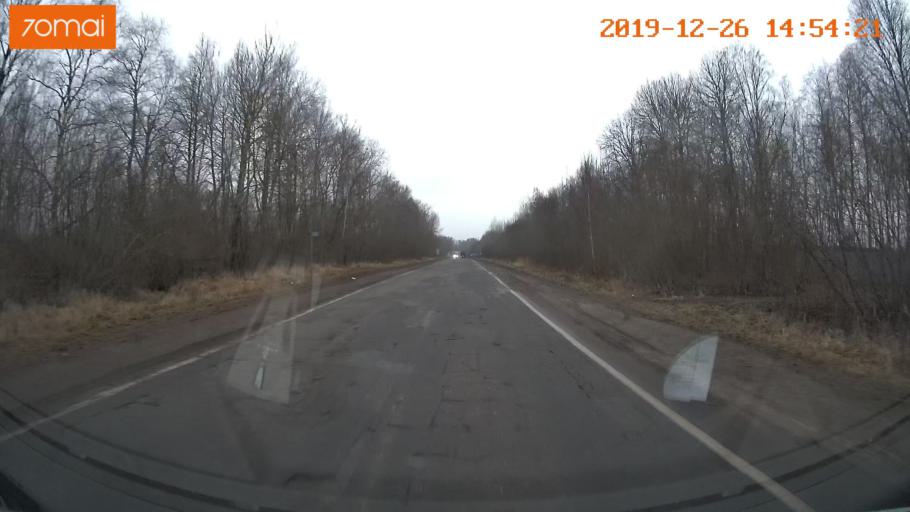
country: RU
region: Jaroslavl
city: Rybinsk
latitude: 58.3079
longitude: 38.8852
